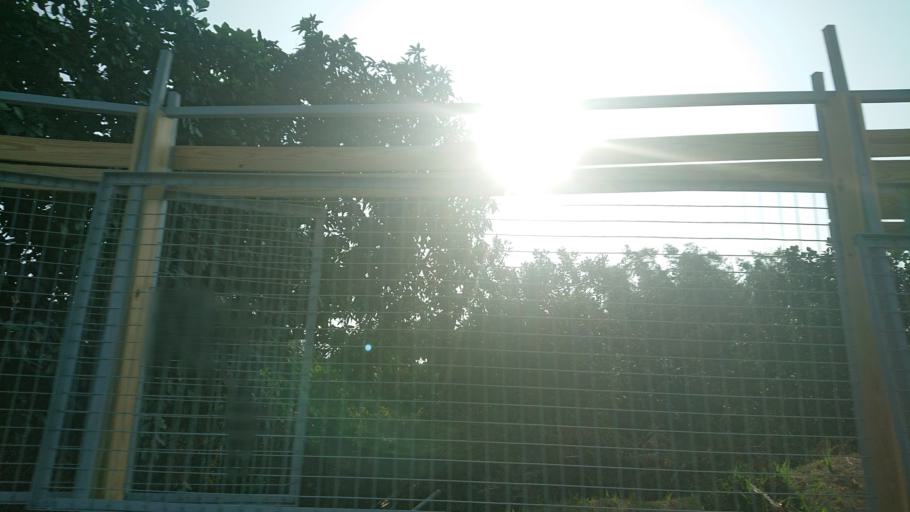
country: TW
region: Taiwan
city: Xinying
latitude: 23.1757
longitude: 120.2603
